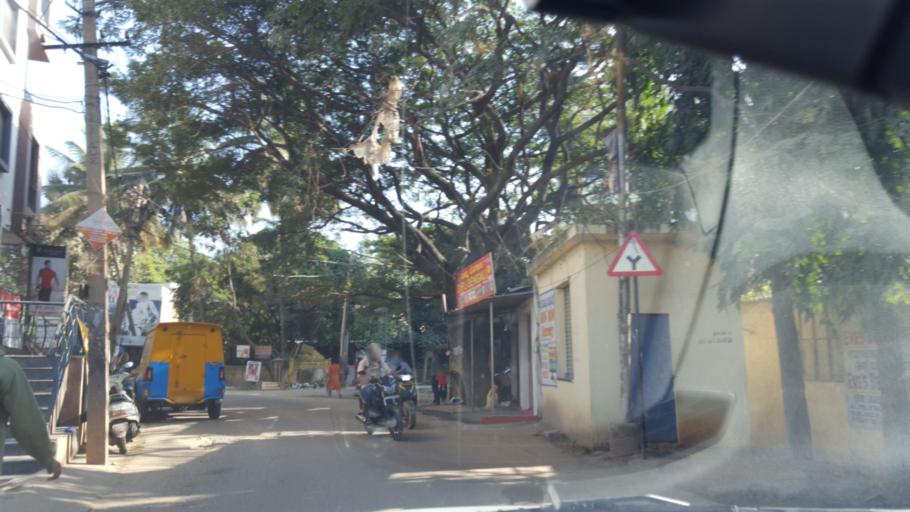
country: IN
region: Karnataka
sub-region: Bangalore Urban
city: Bangalore
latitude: 12.9527
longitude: 77.7058
